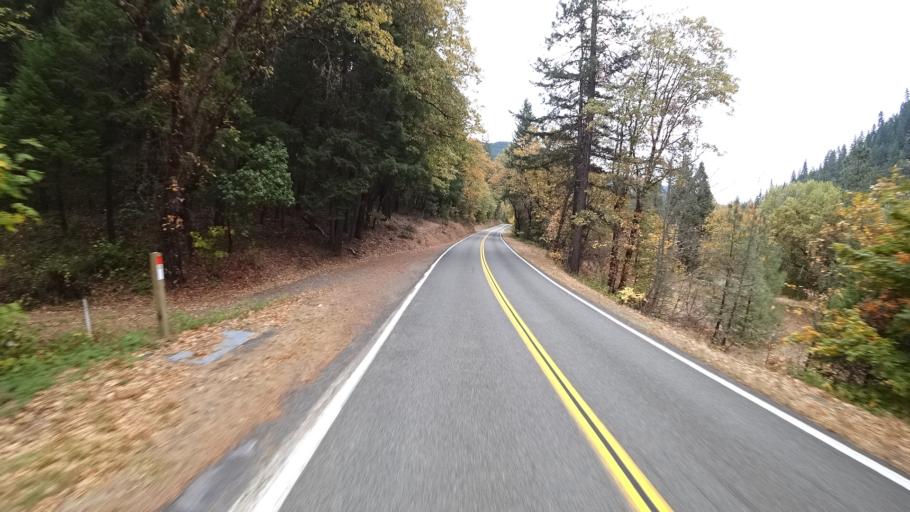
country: US
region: California
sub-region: Siskiyou County
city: Happy Camp
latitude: 41.8569
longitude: -123.3926
